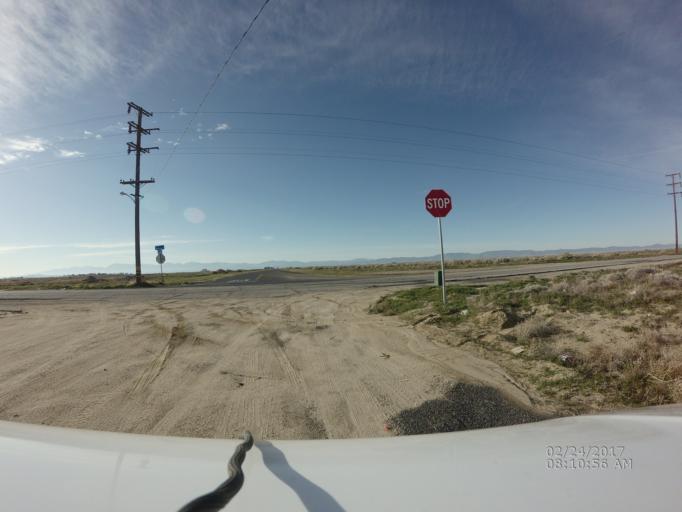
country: US
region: California
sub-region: Los Angeles County
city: Lancaster
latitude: 34.7631
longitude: -118.0413
